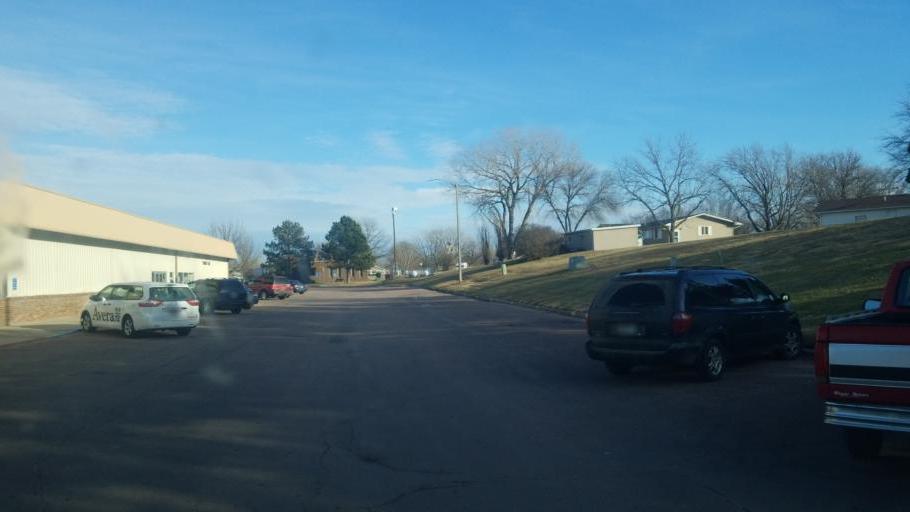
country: US
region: South Dakota
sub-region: Bon Homme County
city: Springfield
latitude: 42.7497
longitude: -98.0325
